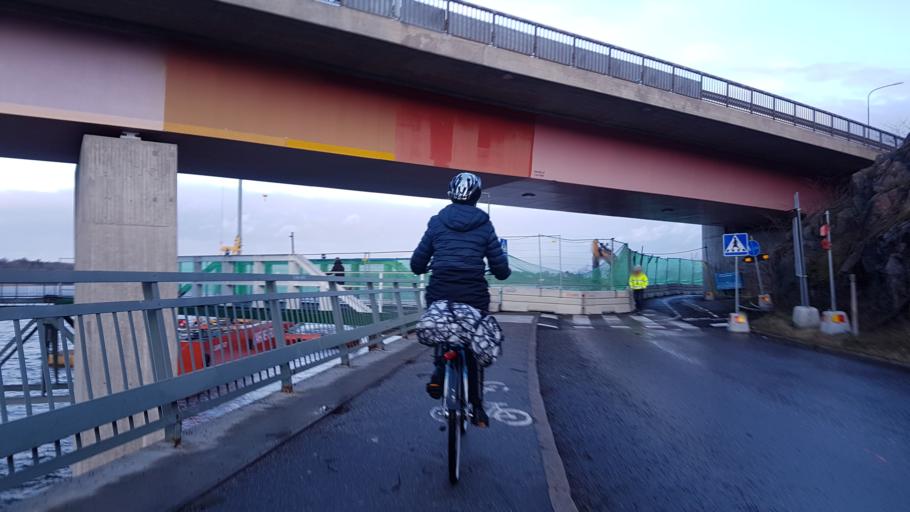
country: SE
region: Stockholm
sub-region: Lidingo
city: Lidingoe
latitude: 59.3632
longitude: 18.1154
